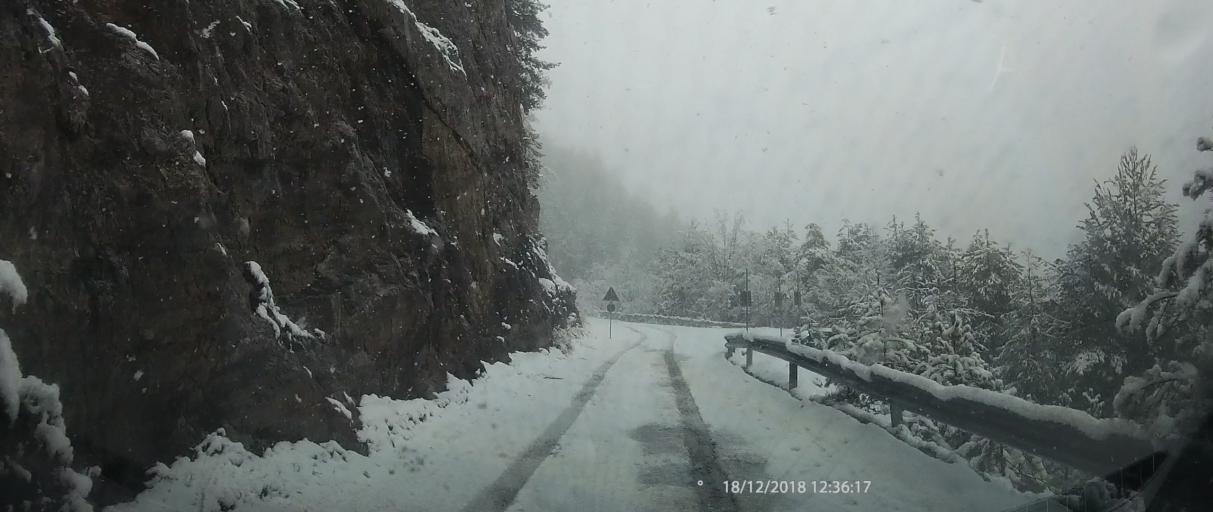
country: GR
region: Central Macedonia
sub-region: Nomos Pierias
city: Litochoro
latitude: 40.0878
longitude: 22.4088
